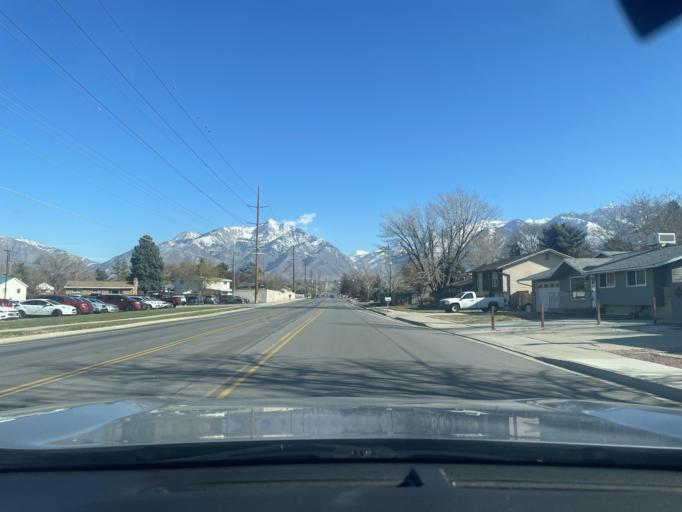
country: US
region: Utah
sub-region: Salt Lake County
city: Sandy City
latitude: 40.5807
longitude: -111.8803
